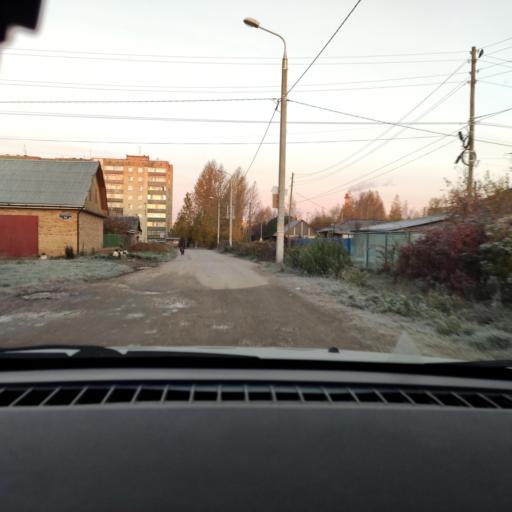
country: RU
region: Perm
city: Perm
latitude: 58.0556
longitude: 56.3583
